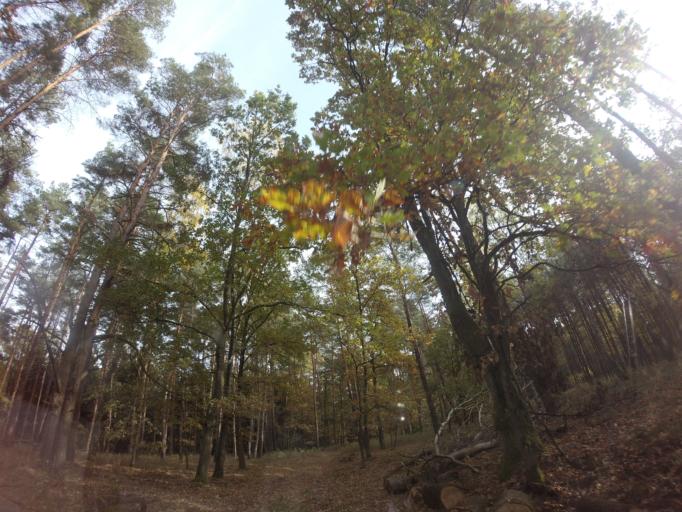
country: PL
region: West Pomeranian Voivodeship
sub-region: Powiat choszczenski
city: Drawno
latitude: 53.2568
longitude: 15.6644
